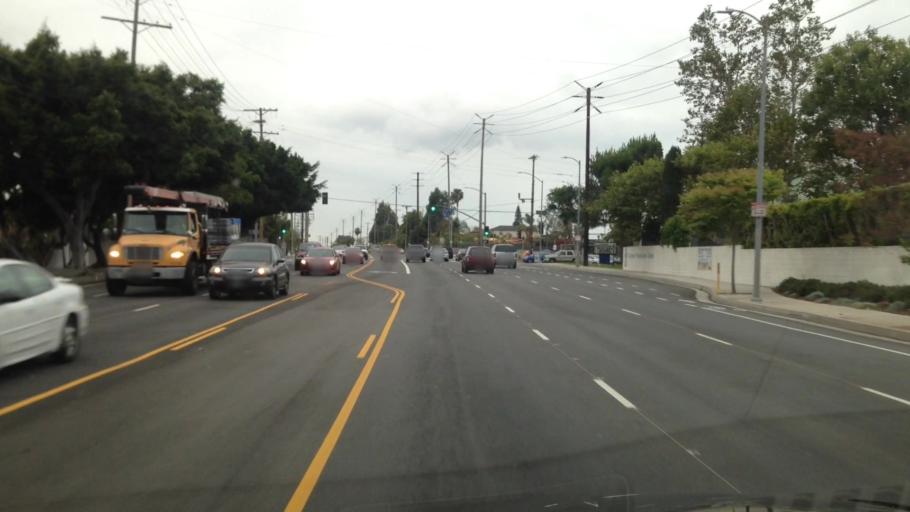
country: US
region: California
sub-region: Los Angeles County
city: Ladera Heights
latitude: 33.9681
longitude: -118.3959
